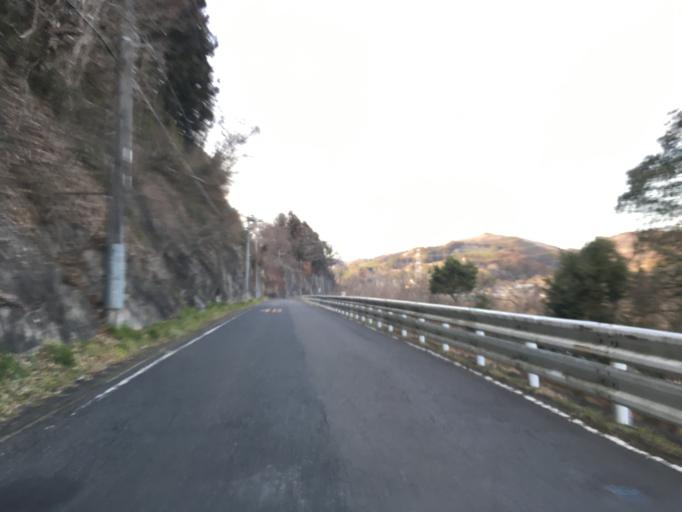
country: JP
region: Ibaraki
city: Daigo
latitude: 36.8111
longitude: 140.3701
